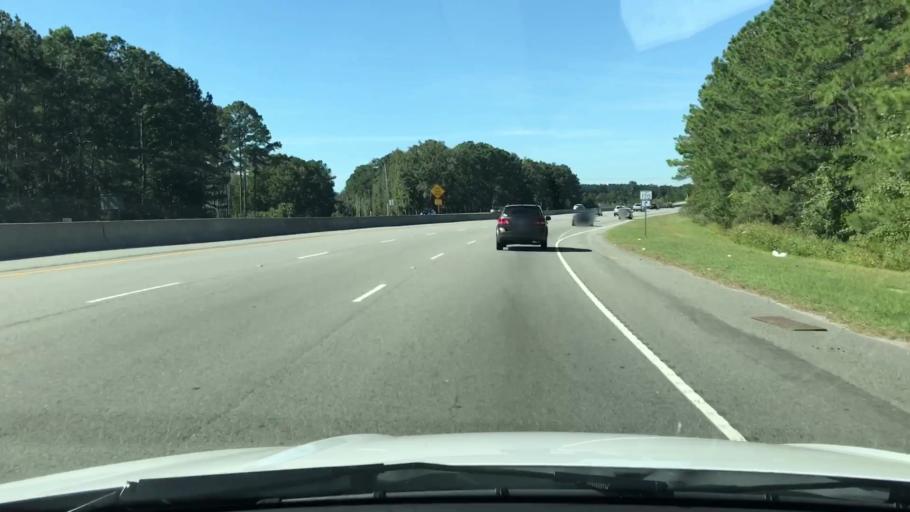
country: US
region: South Carolina
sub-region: Beaufort County
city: Bluffton
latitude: 32.2899
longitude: -80.9312
